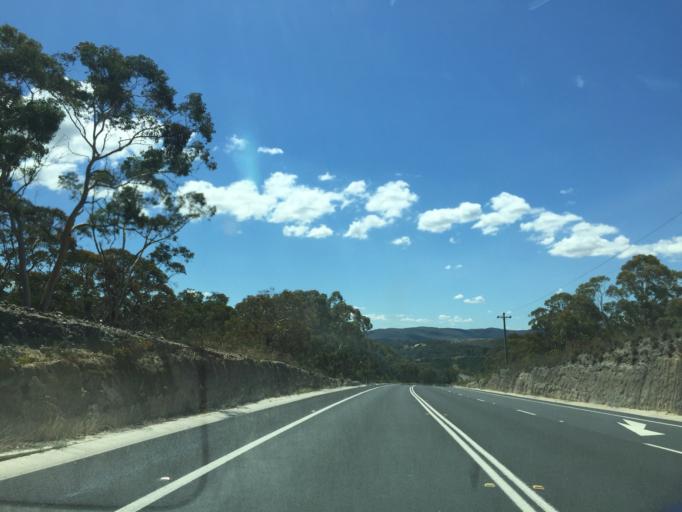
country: AU
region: New South Wales
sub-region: Lithgow
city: Lithgow
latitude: -33.4159
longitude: 150.1002
